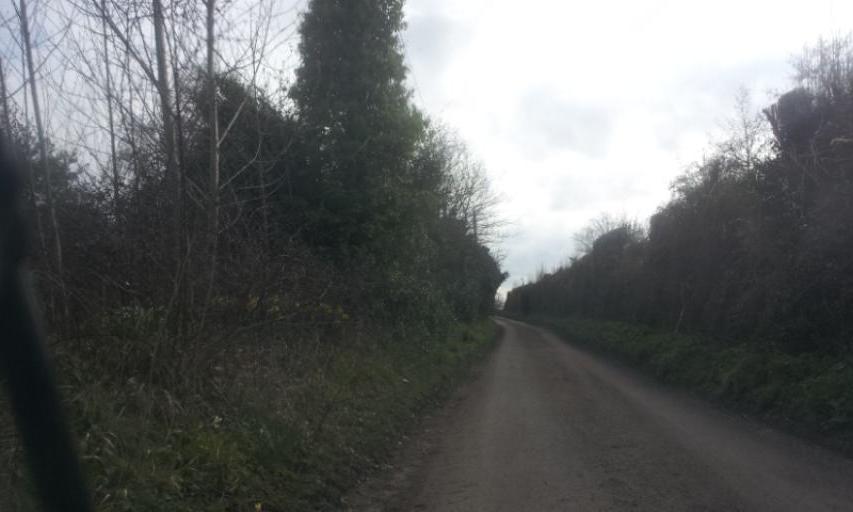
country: GB
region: England
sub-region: Kent
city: Teynham
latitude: 51.3296
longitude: 0.8425
